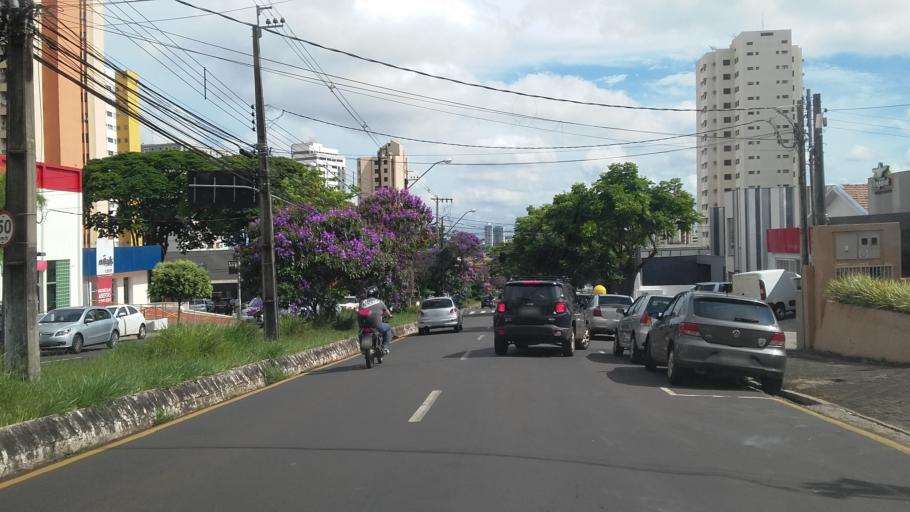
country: BR
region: Parana
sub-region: Londrina
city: Londrina
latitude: -23.3157
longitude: -51.1656
